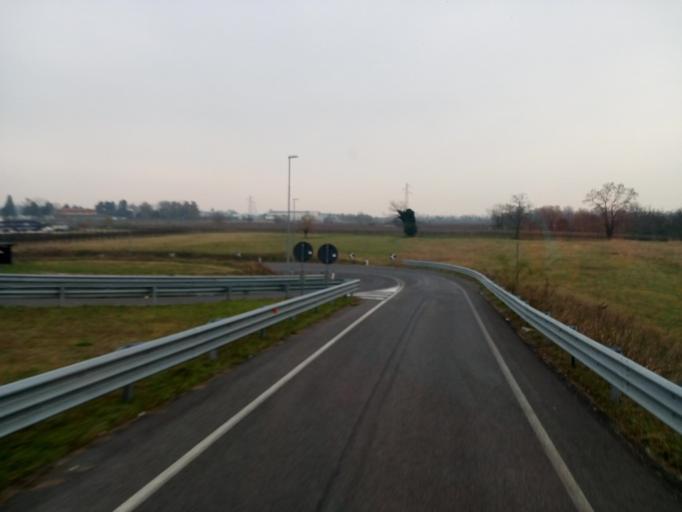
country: IT
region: Friuli Venezia Giulia
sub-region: Provincia di Udine
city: Buttrio
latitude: 46.0159
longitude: 13.3144
